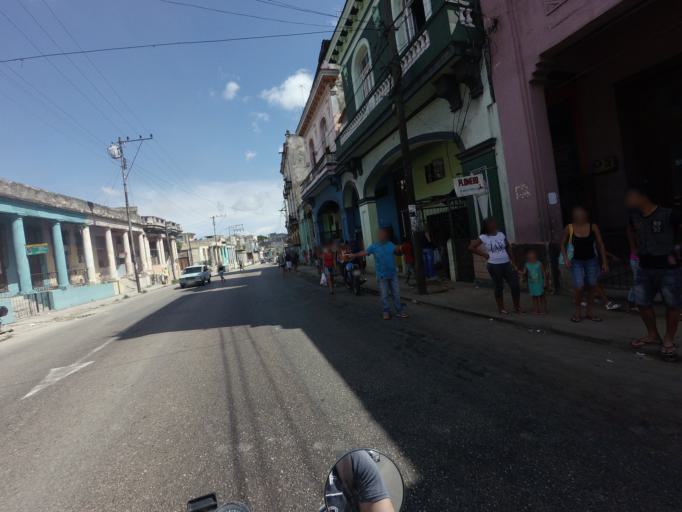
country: TM
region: Balkan
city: Gumdag
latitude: 38.8436
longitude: 54.1734
